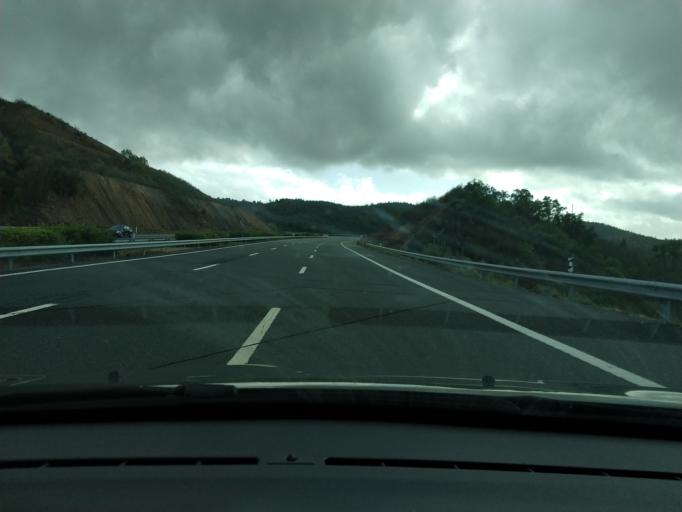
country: PT
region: Faro
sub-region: Silves
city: Sao Bartolomeu de Messines
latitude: 37.4165
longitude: -8.2496
